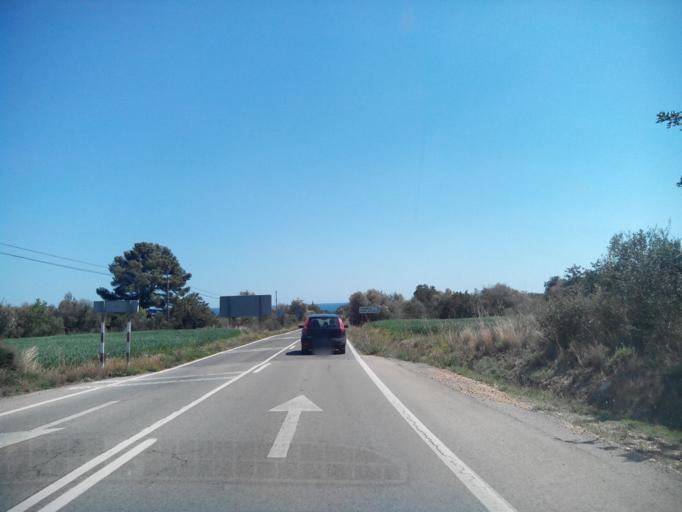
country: ES
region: Catalonia
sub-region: Provincia de Tarragona
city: Vilanova d'Escornalbou
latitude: 41.0757
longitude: 0.9706
